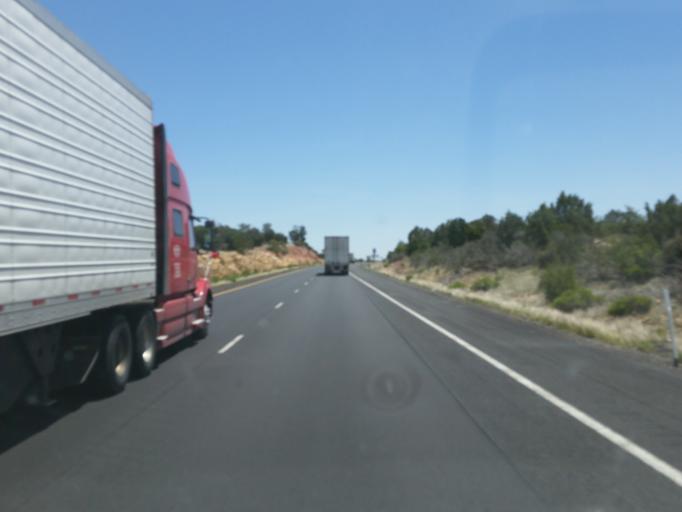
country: US
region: Arizona
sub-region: Coconino County
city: Flagstaff
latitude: 35.2017
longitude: -111.4705
